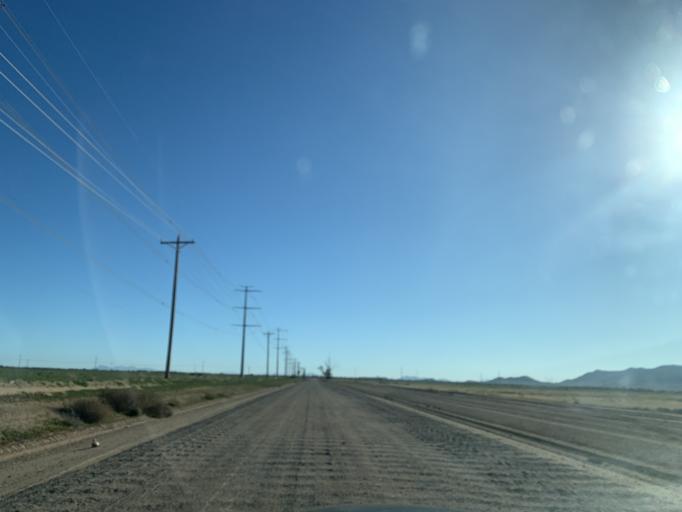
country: US
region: Arizona
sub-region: Pinal County
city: Casa Grande
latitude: 32.8555
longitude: -111.6710
